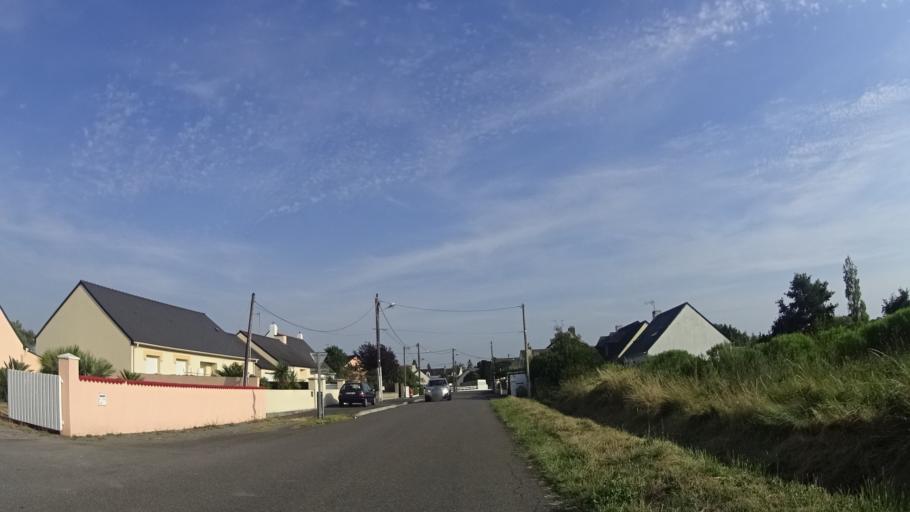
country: FR
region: Pays de la Loire
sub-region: Departement de la Loire-Atlantique
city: Trignac
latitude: 47.3055
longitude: -2.1707
